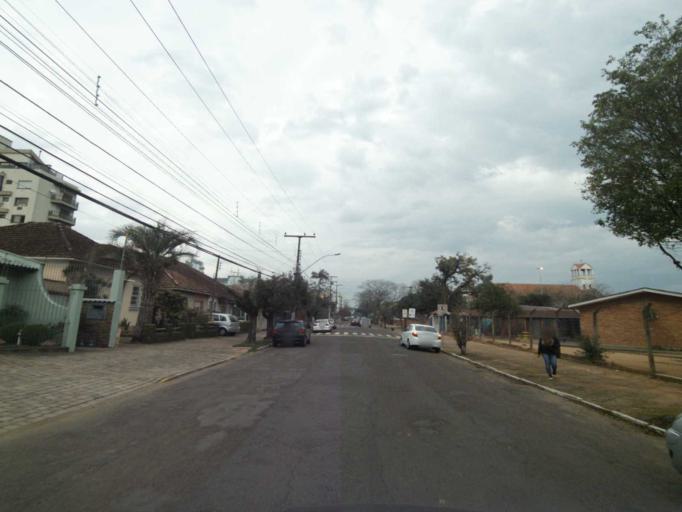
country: BR
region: Rio Grande do Sul
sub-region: Sao Leopoldo
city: Sao Leopoldo
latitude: -29.7723
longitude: -51.1501
